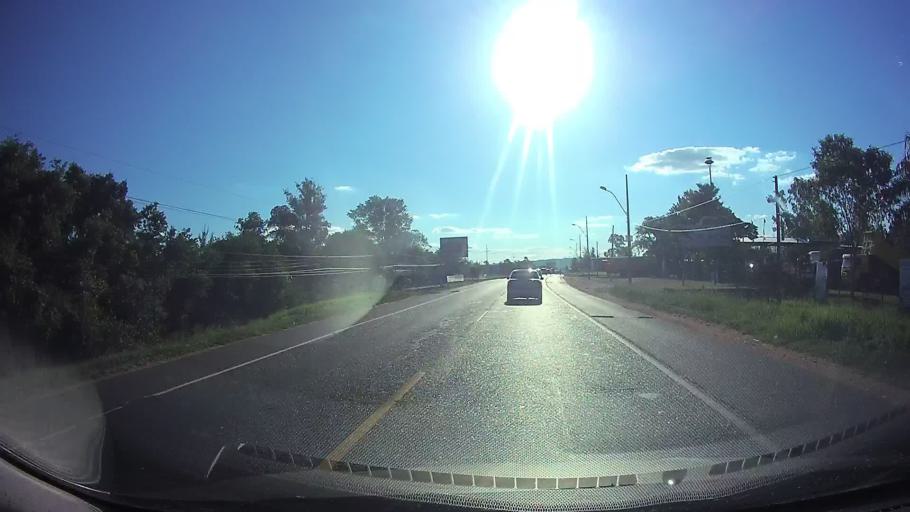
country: PY
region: Central
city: Ypacarai
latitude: -25.3809
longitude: -57.2503
